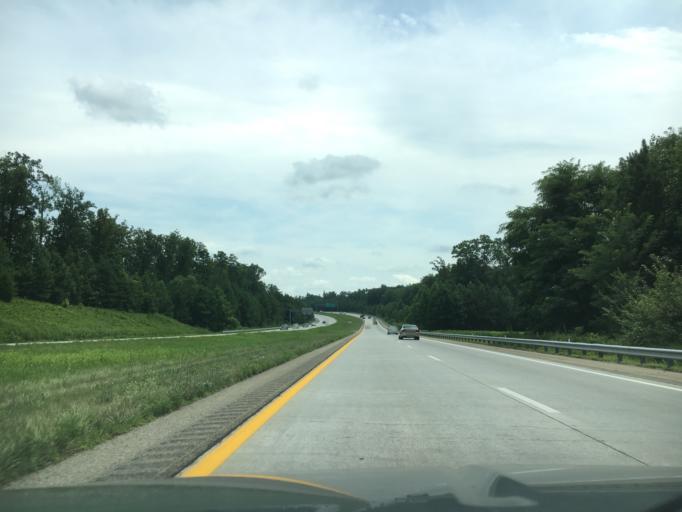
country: US
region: Virginia
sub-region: Chesterfield County
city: Brandermill
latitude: 37.4805
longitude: -77.6624
